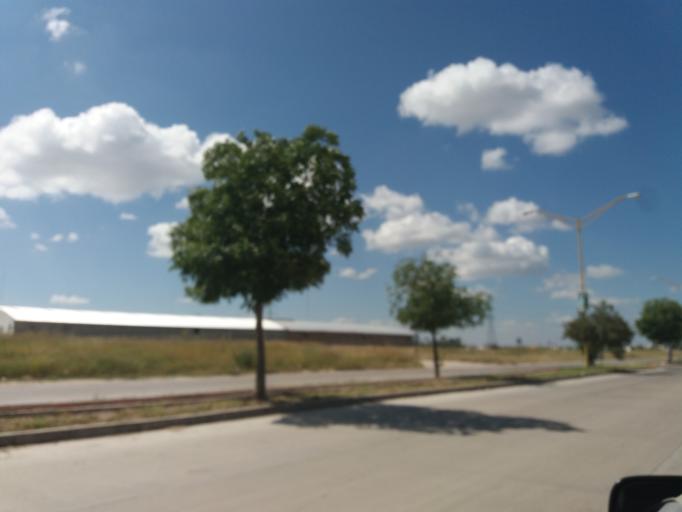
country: MX
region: Aguascalientes
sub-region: Aguascalientes
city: San Sebastian [Fraccionamiento]
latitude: 21.8086
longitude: -102.2874
